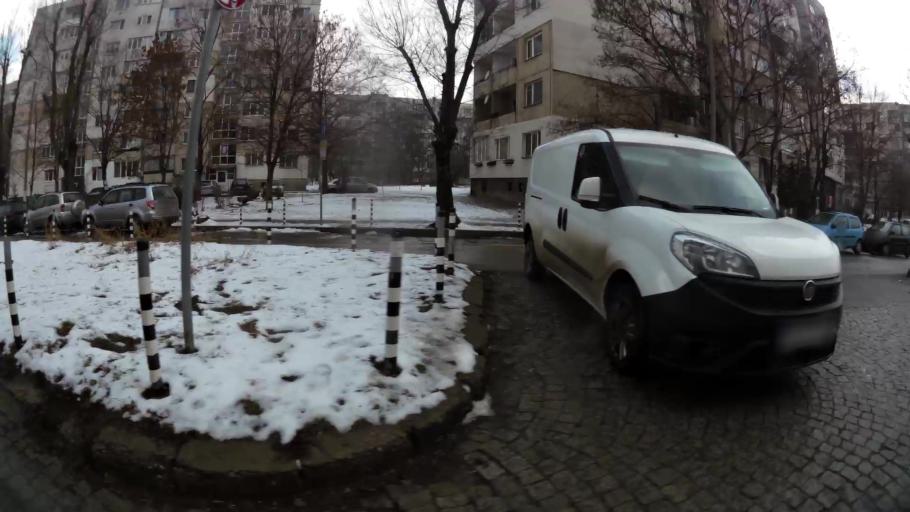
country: BG
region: Sofia-Capital
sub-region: Stolichna Obshtina
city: Sofia
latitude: 42.7082
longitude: 23.2874
